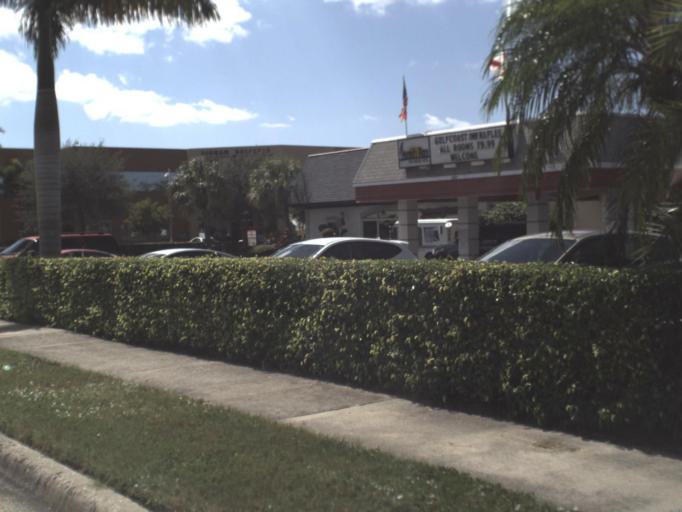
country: US
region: Florida
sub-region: Collier County
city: Naples
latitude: 26.1784
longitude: -81.7999
